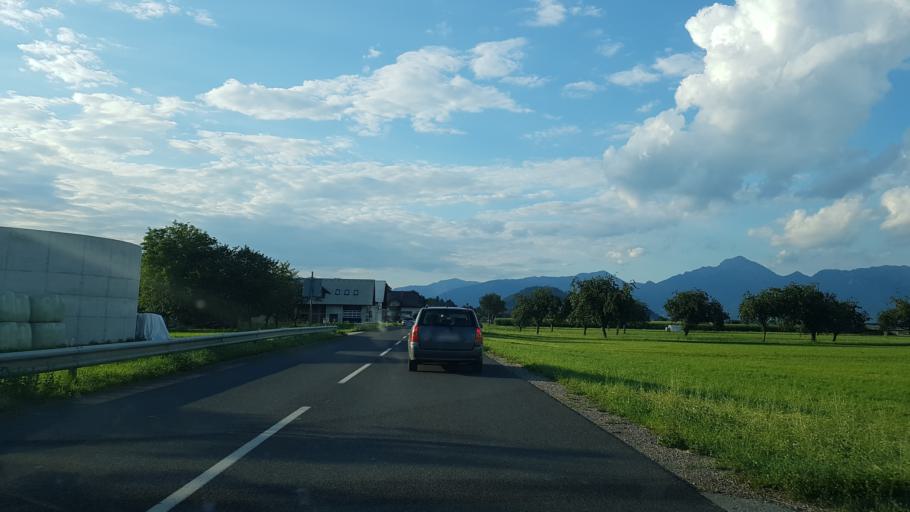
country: SI
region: Skofja Loka
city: Sv. Duh
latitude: 46.1983
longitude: 14.3324
